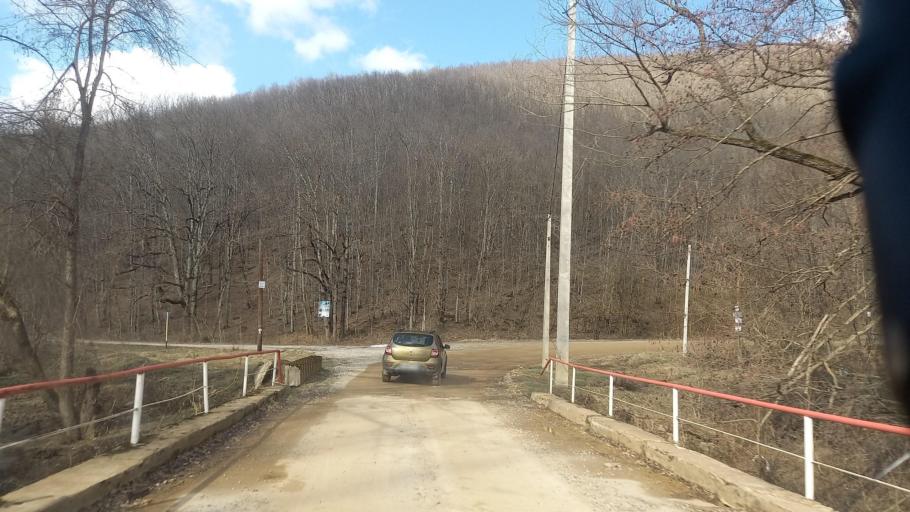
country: RU
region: Krasnodarskiy
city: Smolenskaya
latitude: 44.6050
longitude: 38.8423
